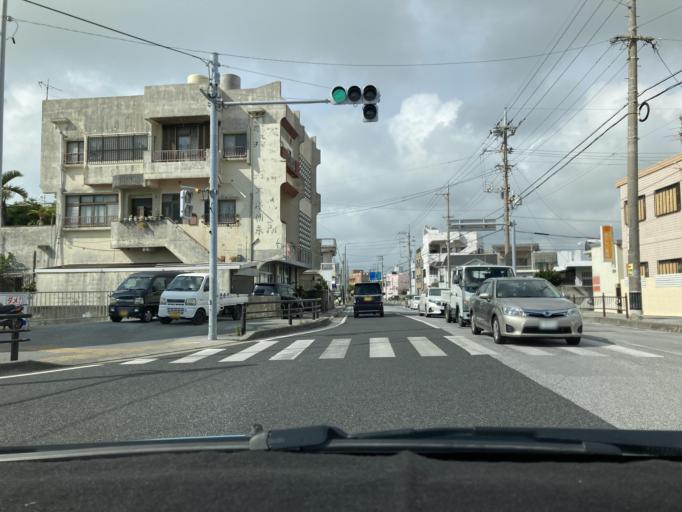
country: JP
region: Okinawa
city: Itoman
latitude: 26.1258
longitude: 127.6695
